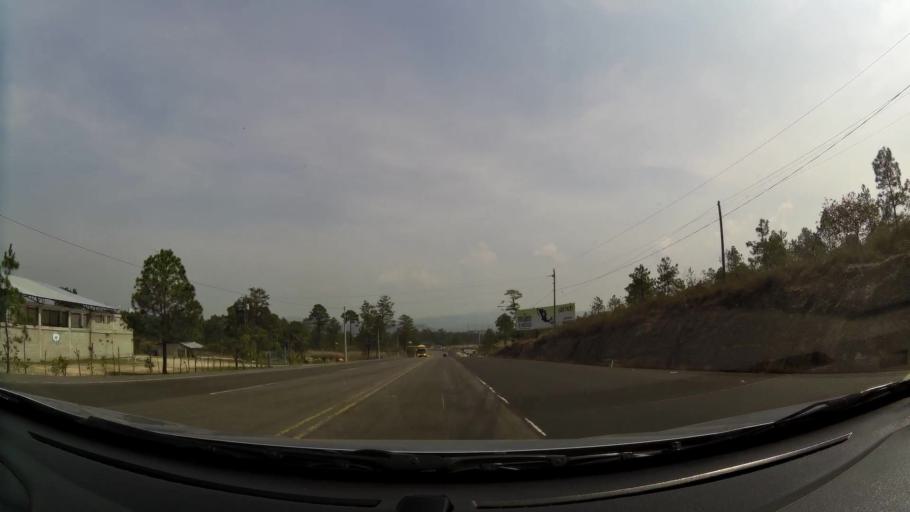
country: HN
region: Comayagua
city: Siguatepeque
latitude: 14.5705
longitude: -87.8304
